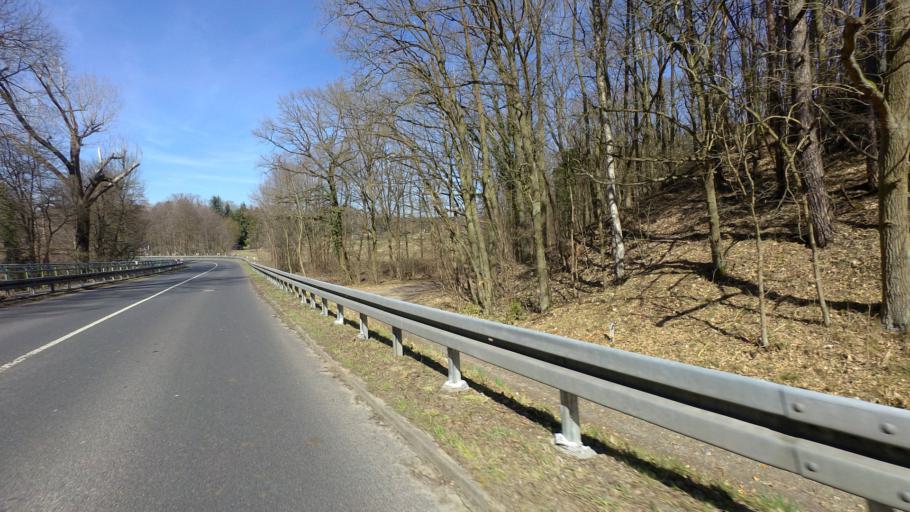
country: DE
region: Brandenburg
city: Furstenwalde
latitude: 52.4007
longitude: 14.0455
